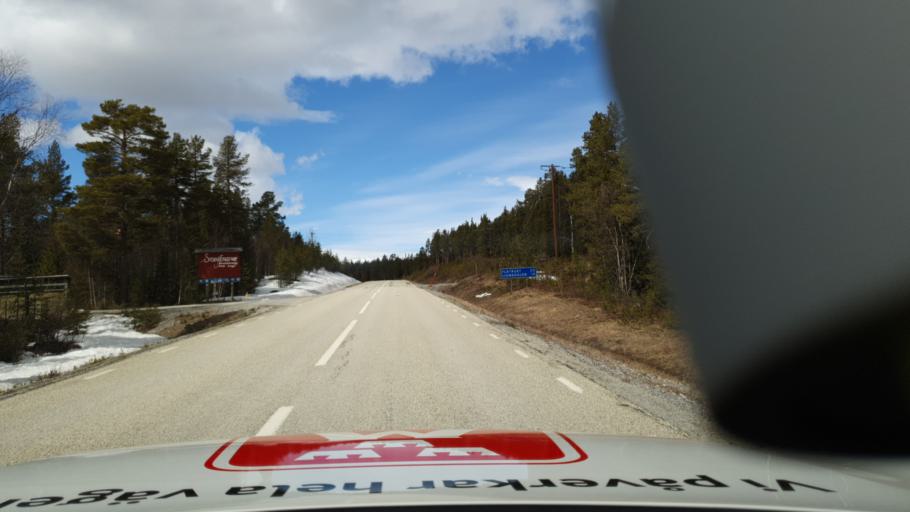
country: SE
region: Jaemtland
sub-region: Are Kommun
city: Are
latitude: 62.8064
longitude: 13.0316
